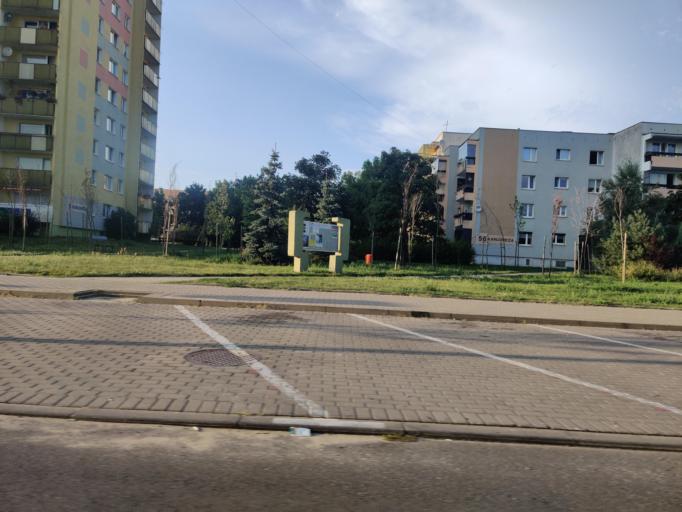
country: PL
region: Greater Poland Voivodeship
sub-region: Konin
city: Konin
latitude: 52.2324
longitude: 18.2552
